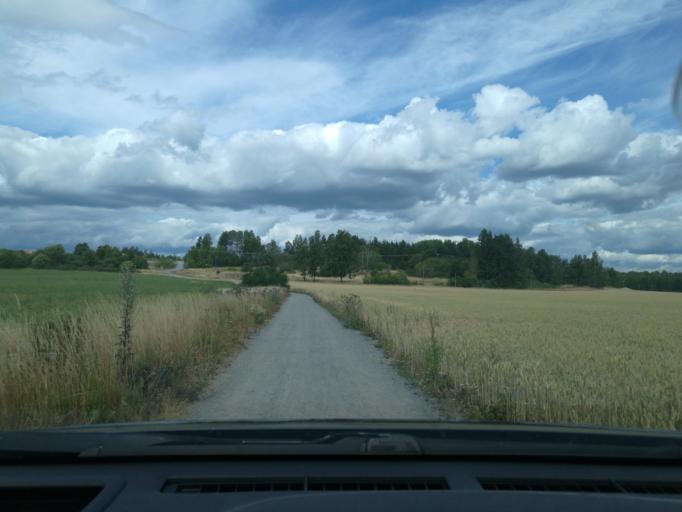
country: SE
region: Stockholm
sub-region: Sigtuna Kommun
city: Marsta
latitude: 59.6166
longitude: 17.8016
